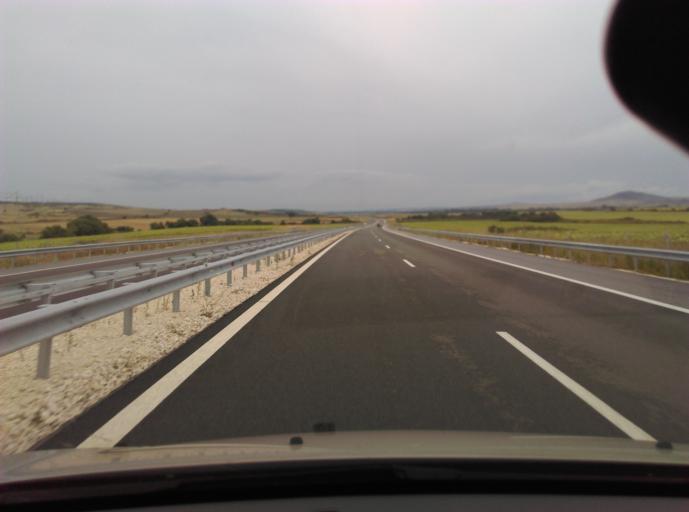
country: BG
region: Stara Zagora
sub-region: Obshtina Chirpan
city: Chirpan
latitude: 42.1285
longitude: 25.3651
